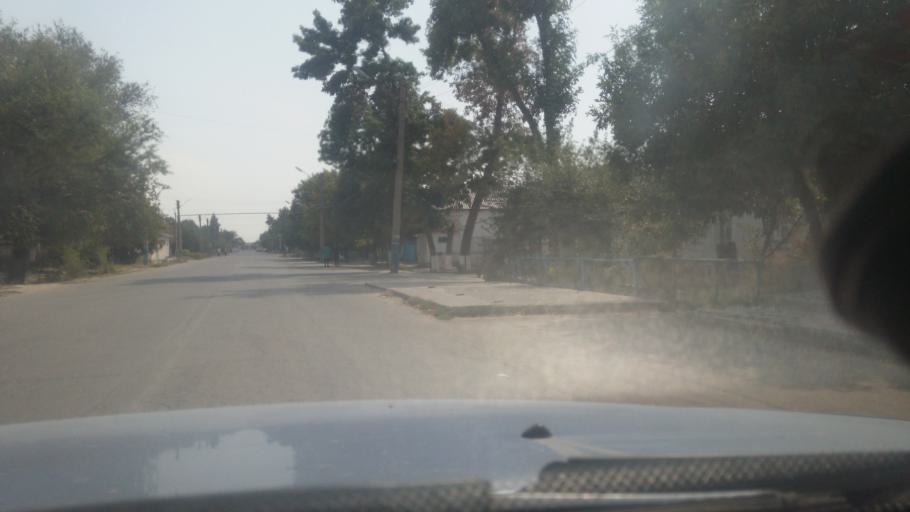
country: UZ
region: Sirdaryo
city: Guliston
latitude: 40.4961
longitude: 68.7824
